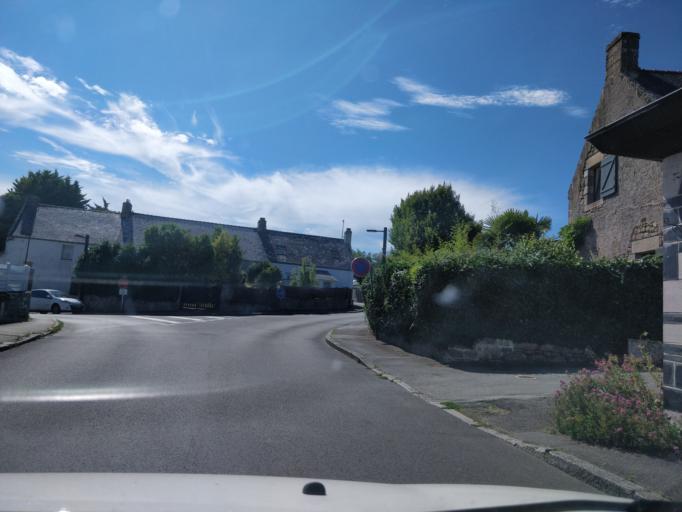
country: FR
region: Brittany
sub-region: Departement du Morbihan
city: Saint-Philibert
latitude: 47.5858
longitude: -2.9994
